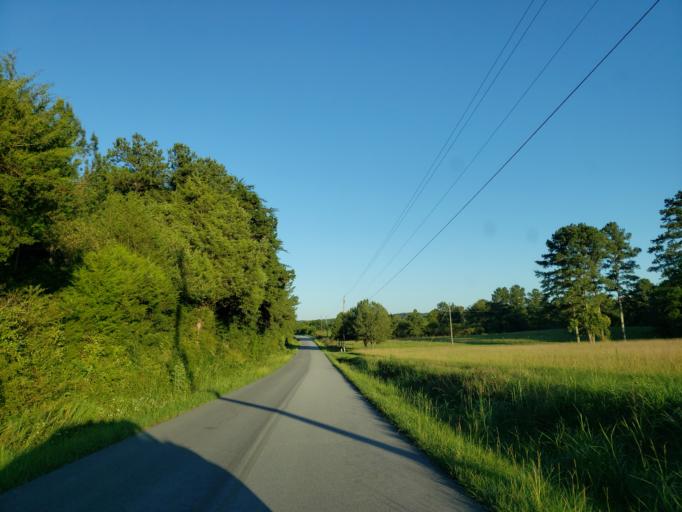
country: US
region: Georgia
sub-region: Bartow County
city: Euharlee
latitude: 34.0770
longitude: -84.9750
